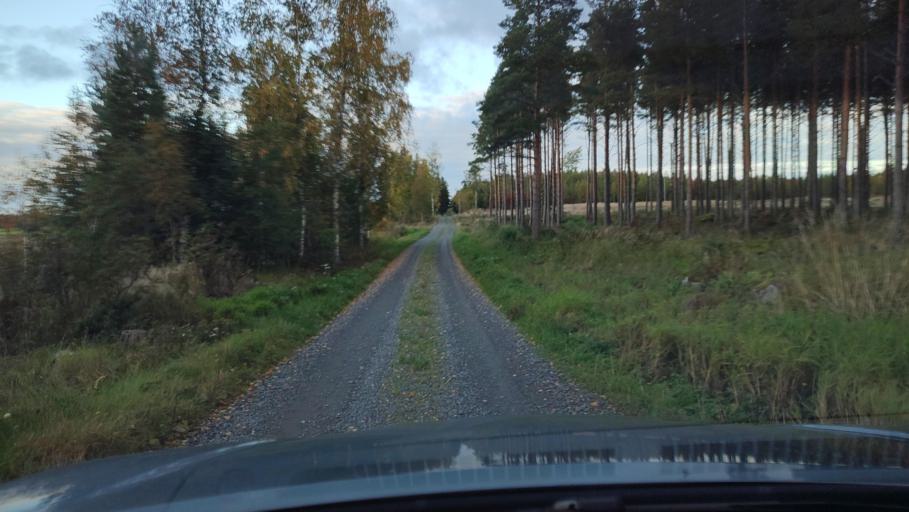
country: FI
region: Ostrobothnia
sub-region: Sydosterbotten
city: Kristinestad
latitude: 62.2479
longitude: 21.4537
